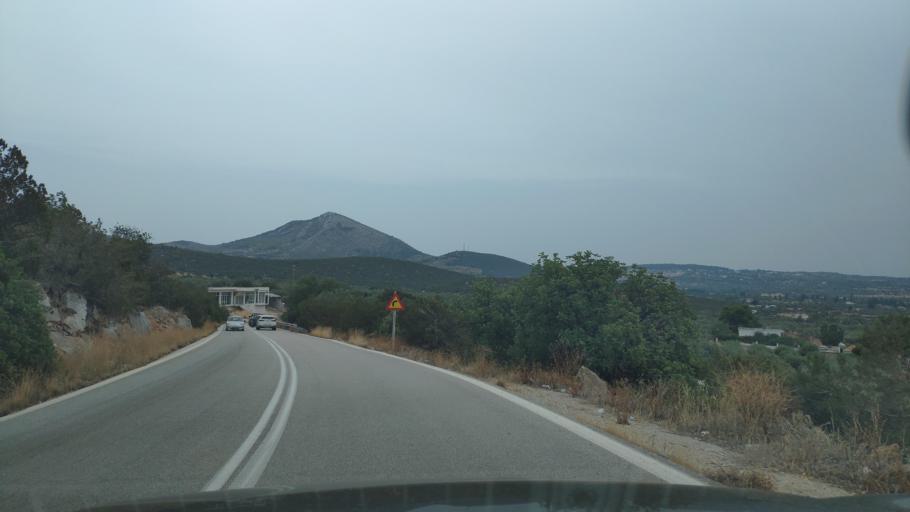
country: GR
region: Peloponnese
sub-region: Nomos Argolidos
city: Koilas
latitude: 37.4225
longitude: 23.1532
